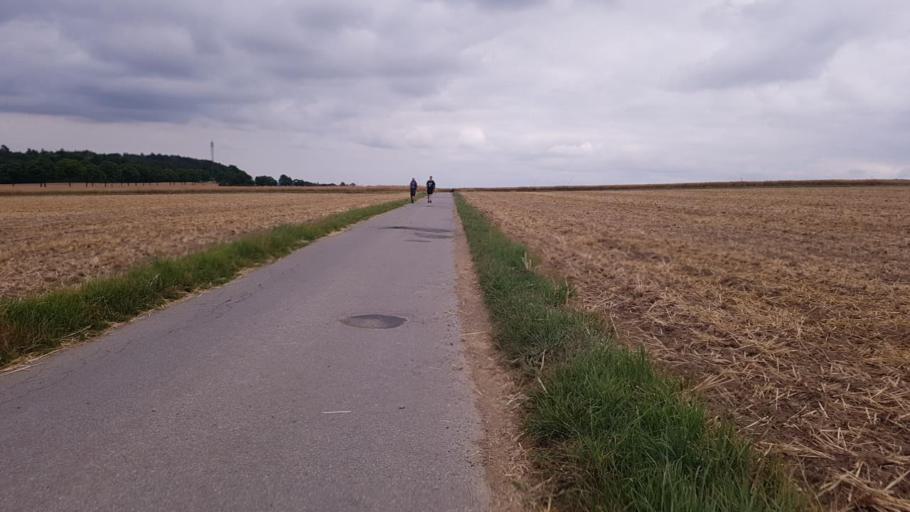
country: DE
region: North Rhine-Westphalia
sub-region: Regierungsbezirk Koln
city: Kreuzau
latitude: 50.7364
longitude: 6.4370
